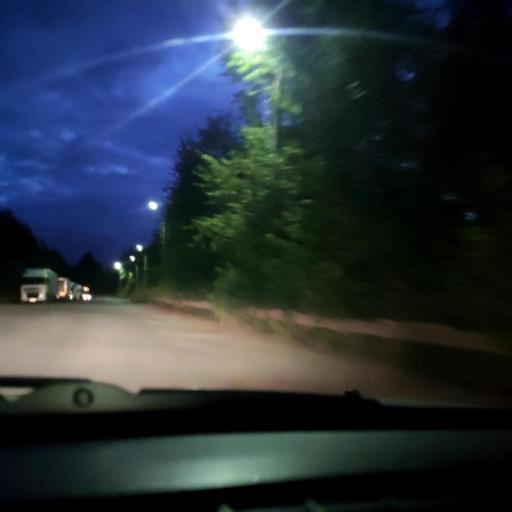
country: RU
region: Perm
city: Polazna
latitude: 58.1537
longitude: 56.4438
